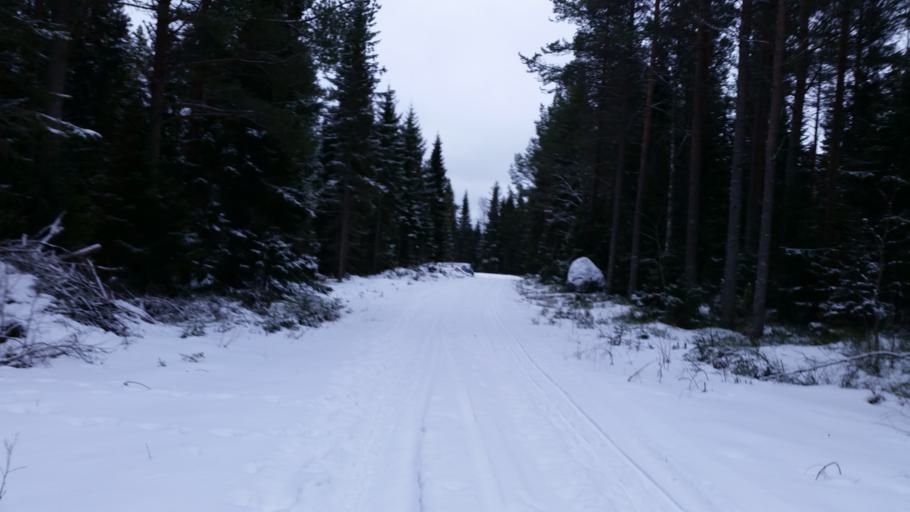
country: SE
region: Vaesterbotten
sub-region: Umea Kommun
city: Saevar
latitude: 63.9161
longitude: 20.7868
